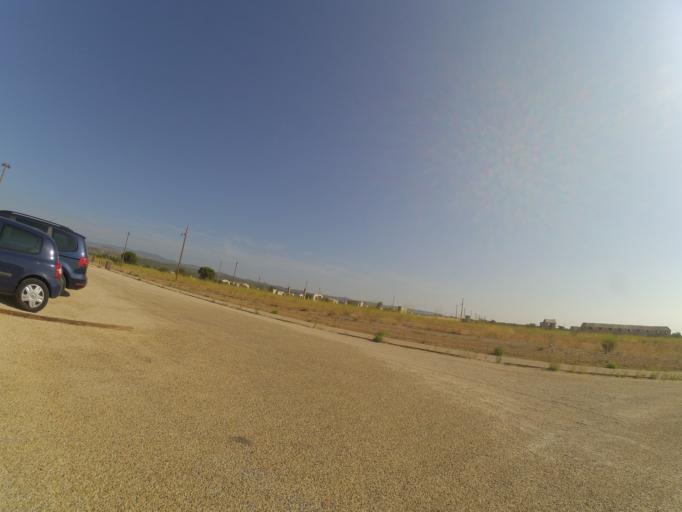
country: FR
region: Languedoc-Roussillon
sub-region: Departement des Pyrenees-Orientales
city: Salses-le-Chateau
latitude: 42.8077
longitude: 2.8905
